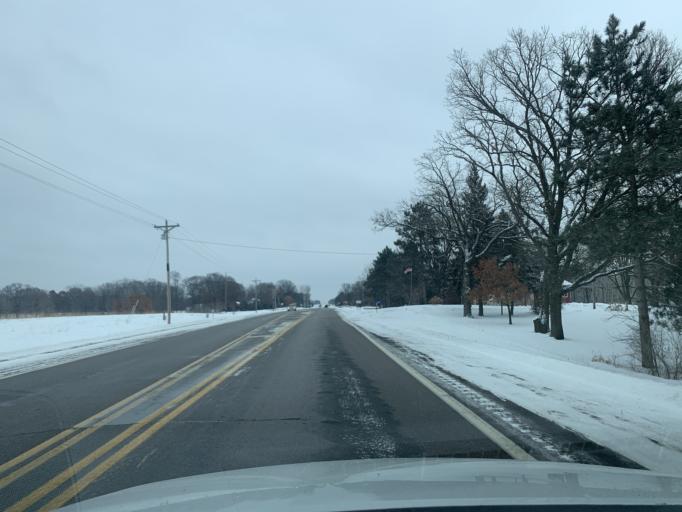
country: US
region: Minnesota
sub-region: Sherburne County
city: Zimmerman
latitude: 45.5016
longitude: -93.5964
